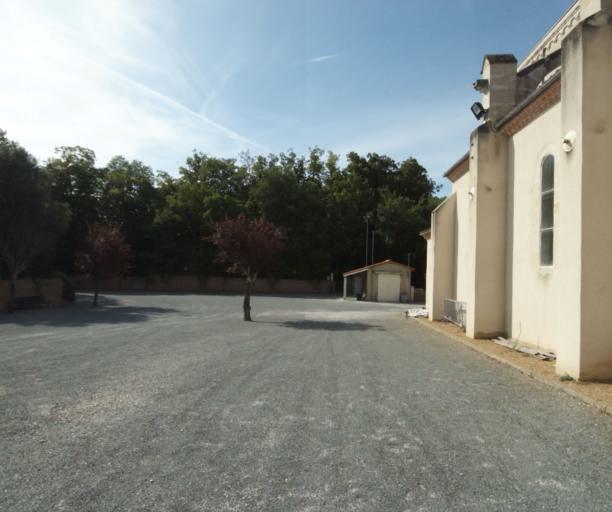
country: FR
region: Midi-Pyrenees
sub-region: Departement du Tarn
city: Soual
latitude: 43.5282
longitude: 2.0646
